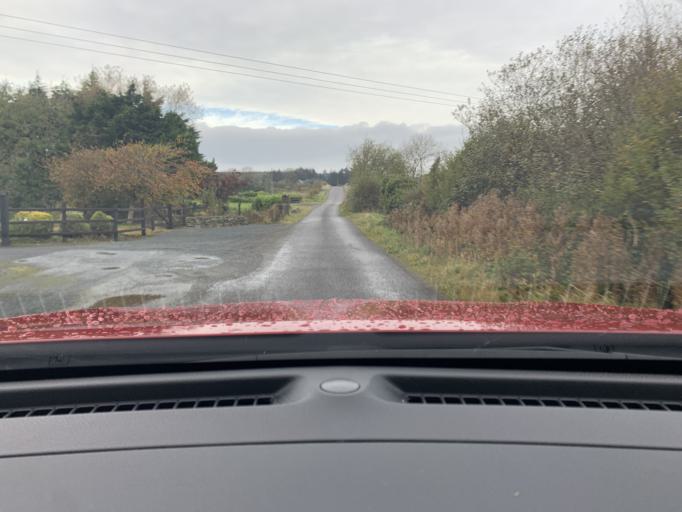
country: IE
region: Connaught
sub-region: Roscommon
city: Ballaghaderreen
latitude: 53.9131
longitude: -8.5656
